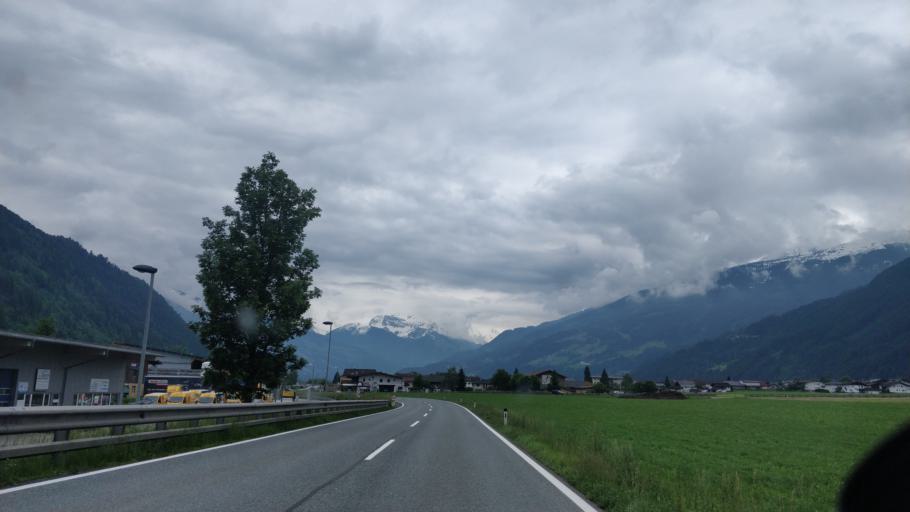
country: AT
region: Tyrol
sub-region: Politischer Bezirk Schwaz
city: Uderns
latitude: 47.3335
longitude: 11.8616
